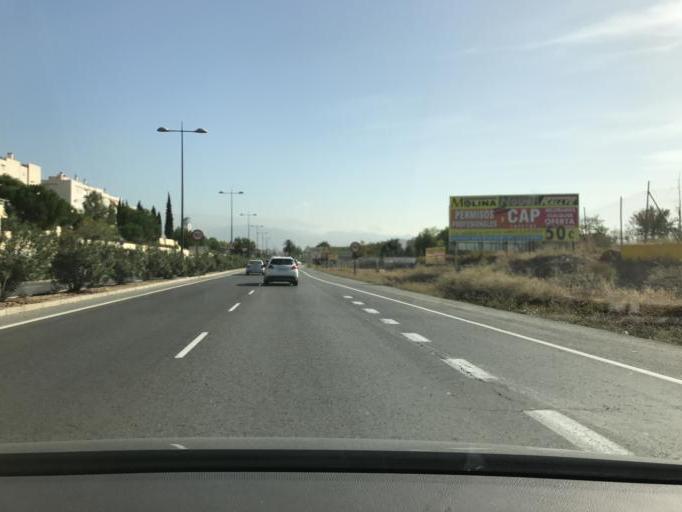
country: ES
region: Andalusia
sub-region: Provincia de Granada
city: Maracena
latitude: 37.2084
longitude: -3.6215
